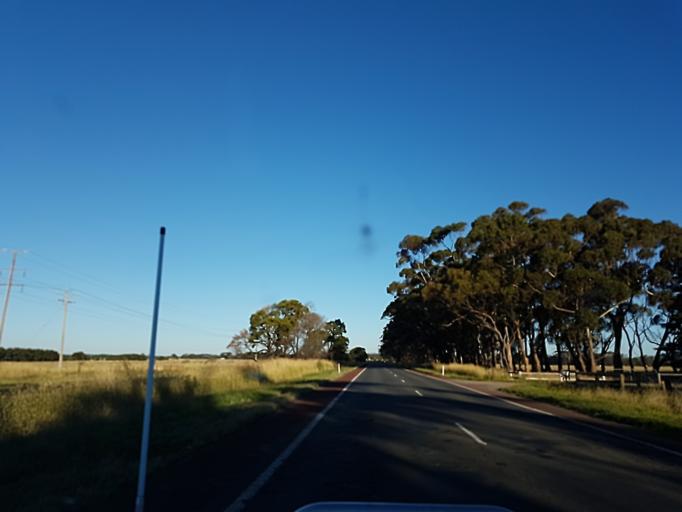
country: AU
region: Victoria
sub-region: Warrnambool
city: Allansford
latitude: -38.2157
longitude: 143.0198
